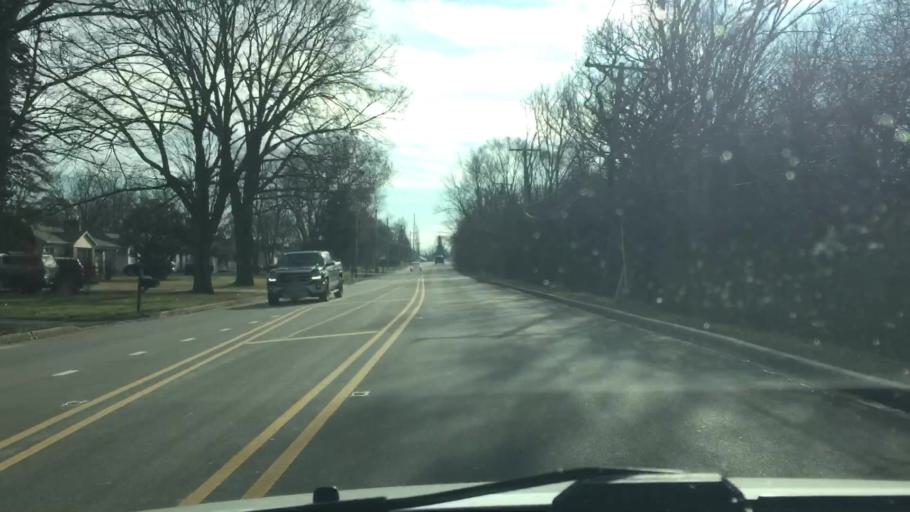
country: US
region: Illinois
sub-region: Kane County
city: Batavia
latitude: 41.8656
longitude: -88.3066
